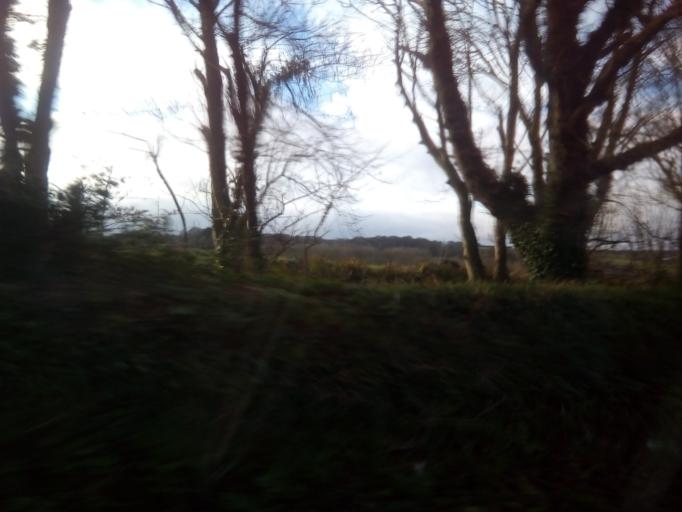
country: IE
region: Leinster
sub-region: Fingal County
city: Skerries
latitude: 53.5724
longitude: -6.1328
